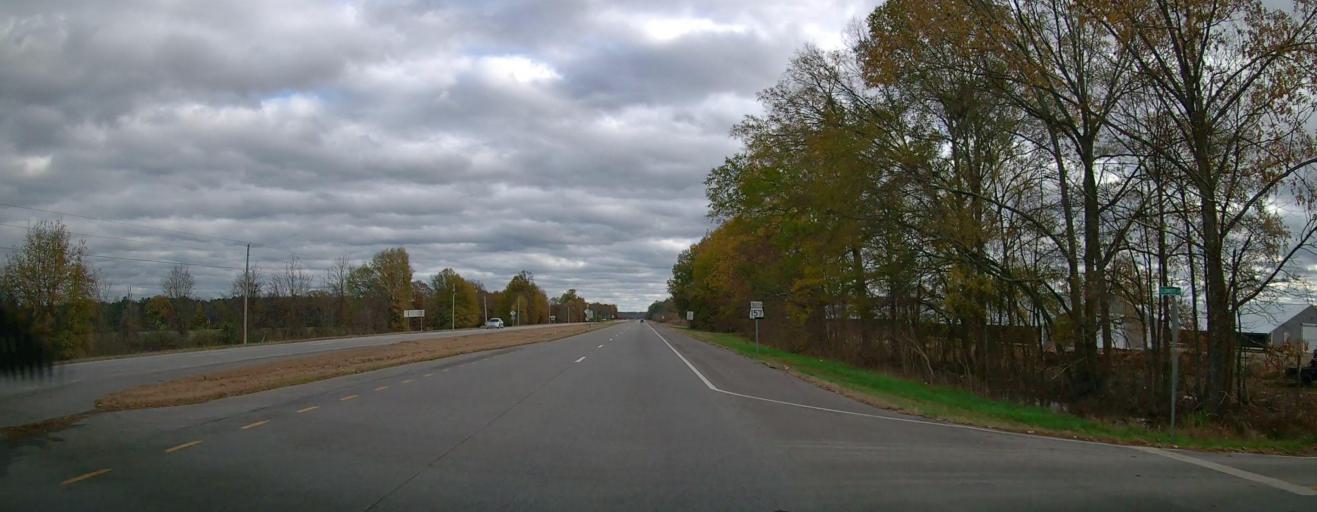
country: US
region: Alabama
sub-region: Lawrence County
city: Town Creek
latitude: 34.6523
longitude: -87.5265
